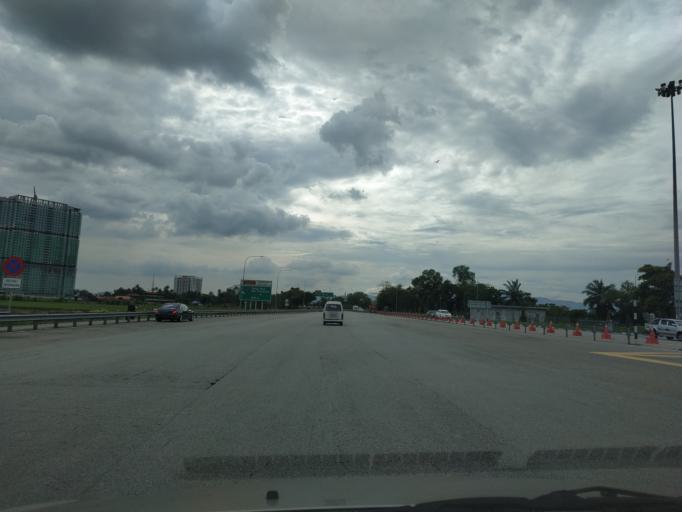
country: MY
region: Penang
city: Perai
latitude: 5.3981
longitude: 100.4241
